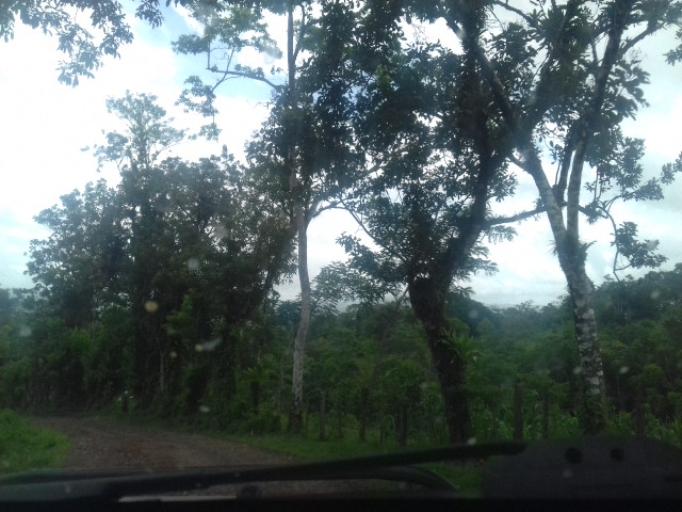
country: NI
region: Matagalpa
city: Matiguas
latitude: 12.9389
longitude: -85.3686
